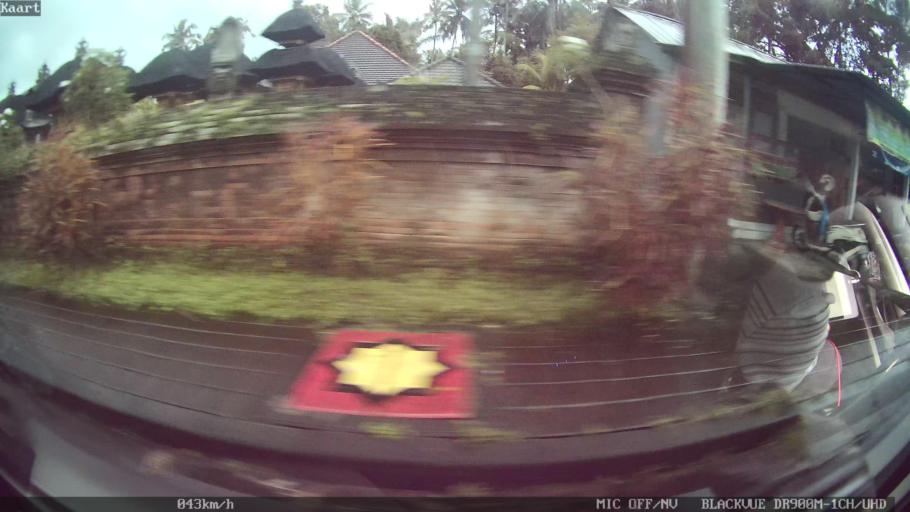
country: ID
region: Bali
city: Banjar Teguan
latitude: -8.5040
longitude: 115.2310
